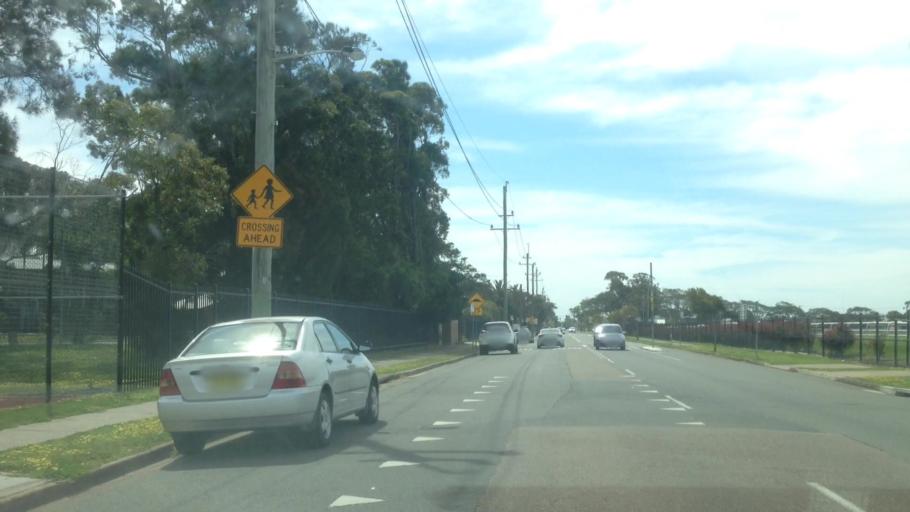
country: AU
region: New South Wales
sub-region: Newcastle
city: Broadmeadow
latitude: -32.9304
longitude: 151.7362
